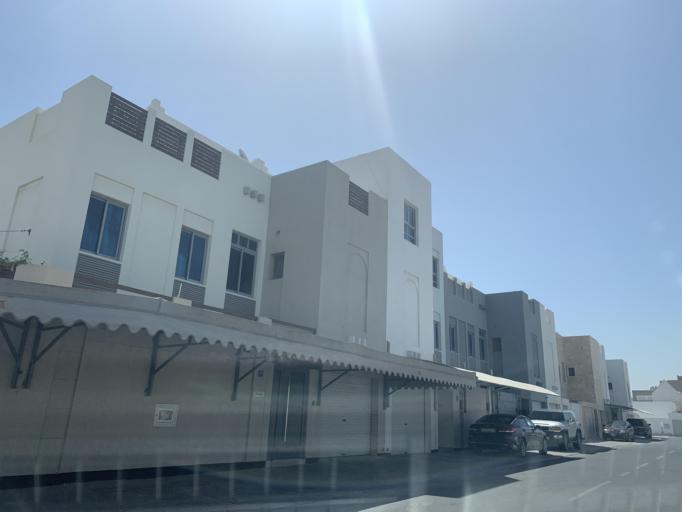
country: BH
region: Northern
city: Ar Rifa'
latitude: 26.1325
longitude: 50.5817
